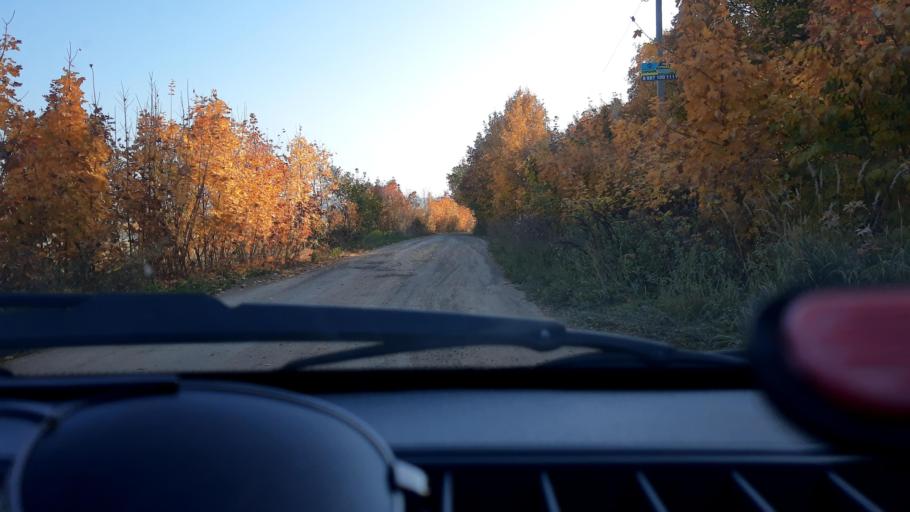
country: RU
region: Bashkortostan
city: Karmaskaly
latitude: 54.3751
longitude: 55.9105
